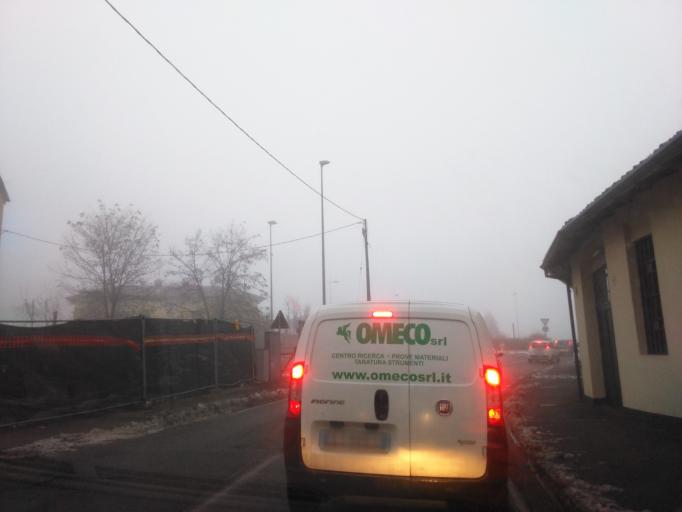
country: IT
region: Lombardy
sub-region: Provincia di Brescia
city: Capriano del Colle
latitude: 45.4704
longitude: 10.1224
